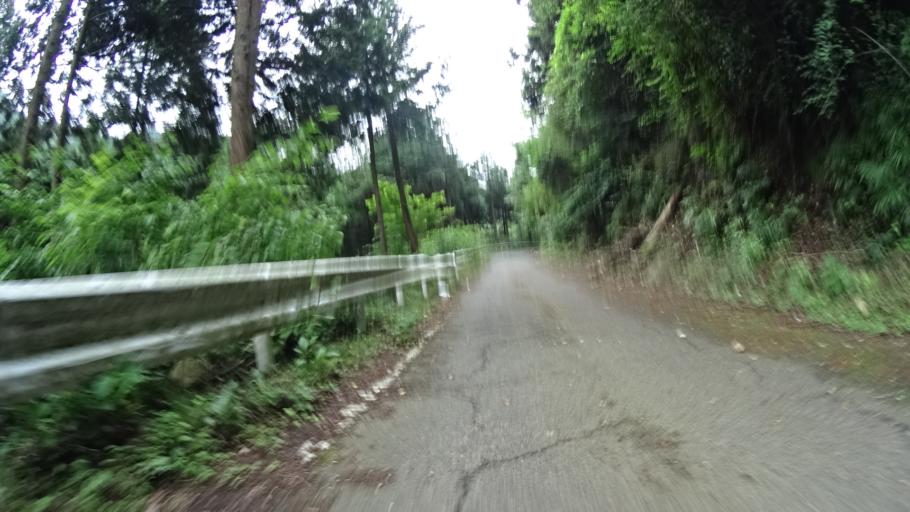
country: JP
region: Kanagawa
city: Atsugi
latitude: 35.5022
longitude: 139.2722
